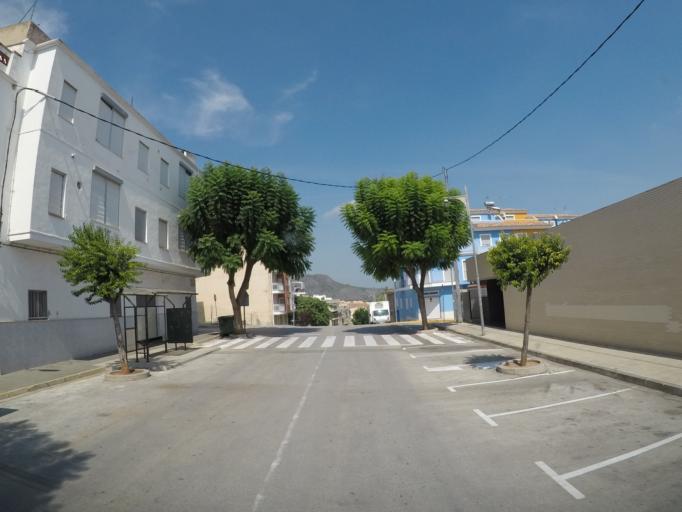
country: ES
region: Valencia
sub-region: Provincia de Alicante
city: Pego
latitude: 38.8418
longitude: -0.1130
